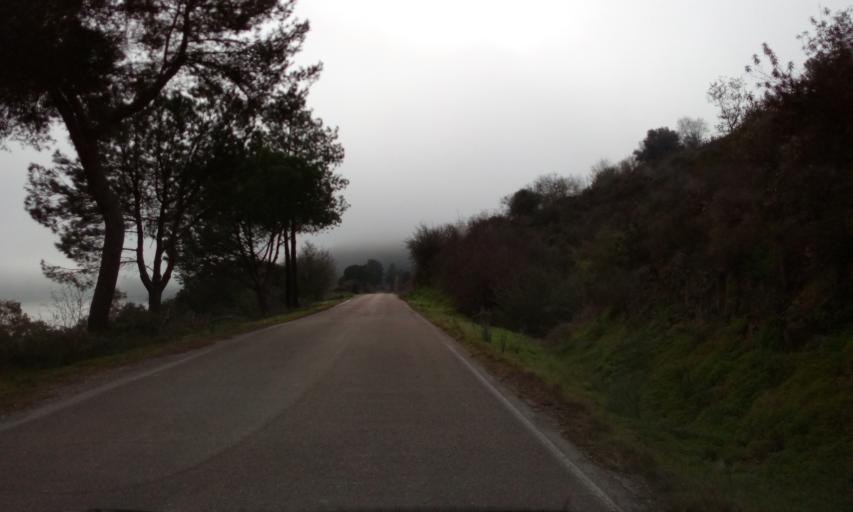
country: ES
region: Andalusia
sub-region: Provincia de Huelva
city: Sanlucar de Guadiana
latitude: 37.4643
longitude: -7.4691
